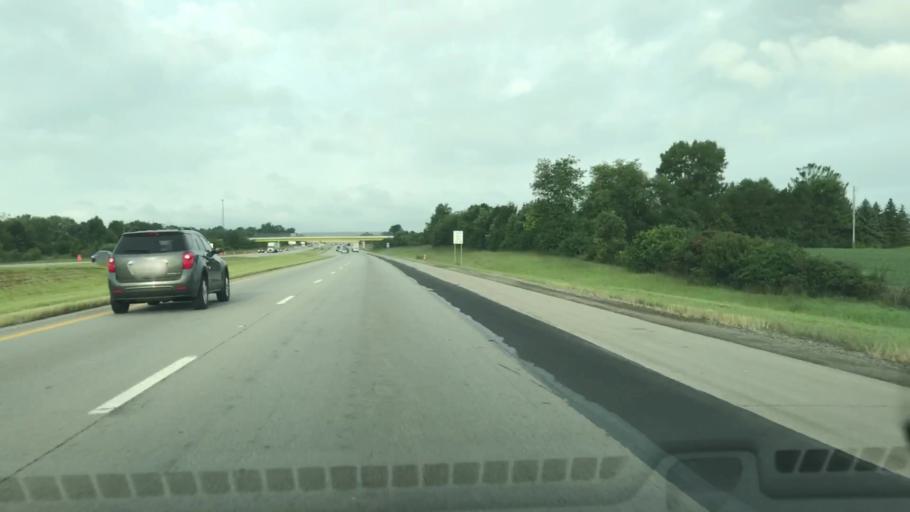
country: US
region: Ohio
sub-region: Clark County
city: Springfield
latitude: 39.8953
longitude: -83.8621
